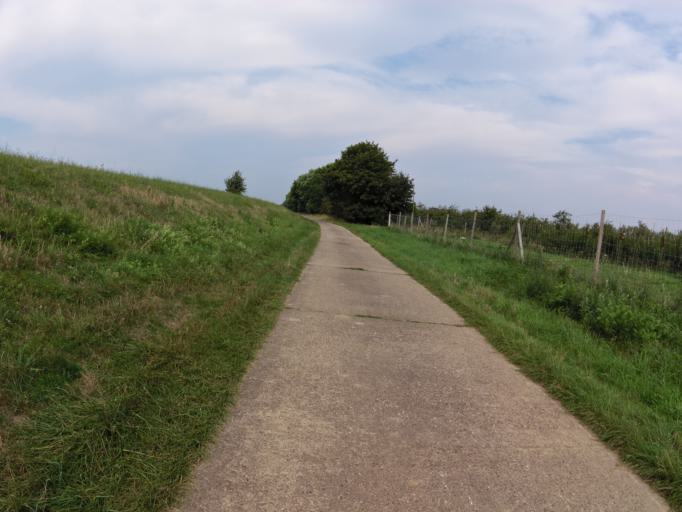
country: DE
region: Lower Saxony
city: Landesbergen
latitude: 52.5625
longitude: 9.1146
